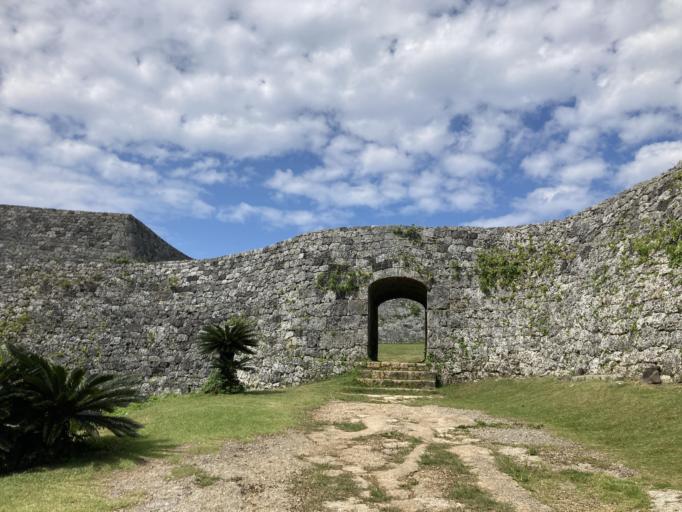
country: JP
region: Okinawa
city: Ishikawa
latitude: 26.4080
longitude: 127.7419
